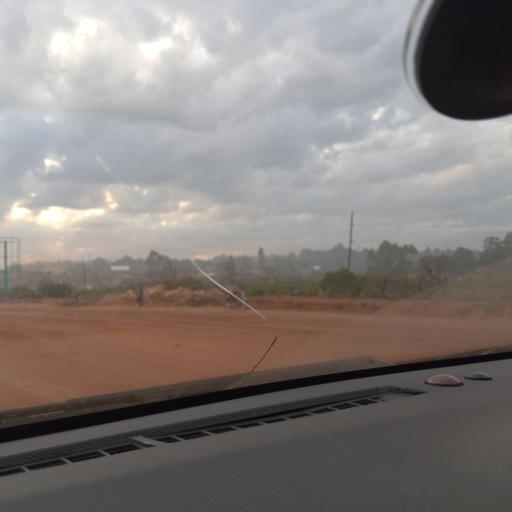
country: UG
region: Central Region
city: Masaka
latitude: -0.3285
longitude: 31.7487
